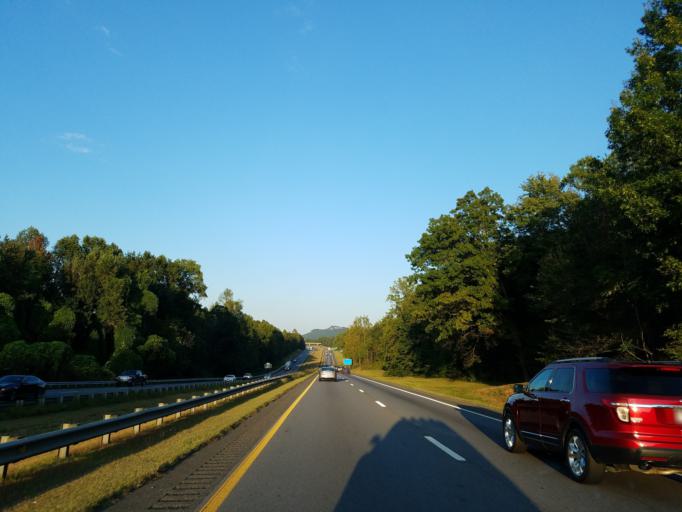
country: US
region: North Carolina
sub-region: Cleveland County
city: White Plains
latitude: 35.1972
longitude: -81.3836
